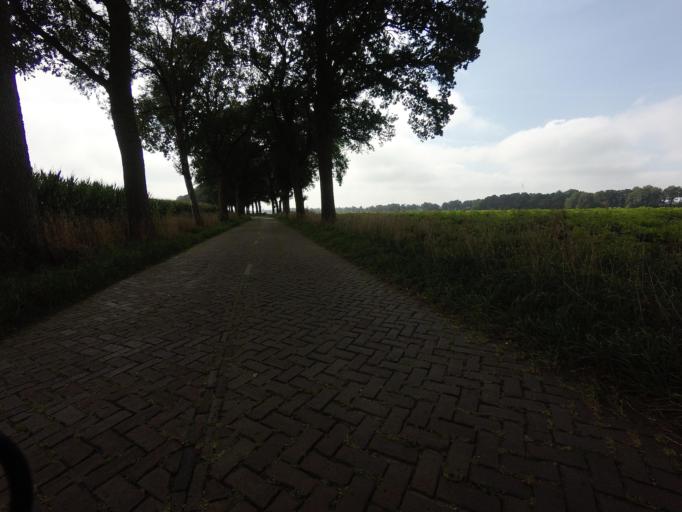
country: NL
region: Drenthe
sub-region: Gemeente Tynaarlo
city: Vries
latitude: 53.1068
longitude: 6.5372
